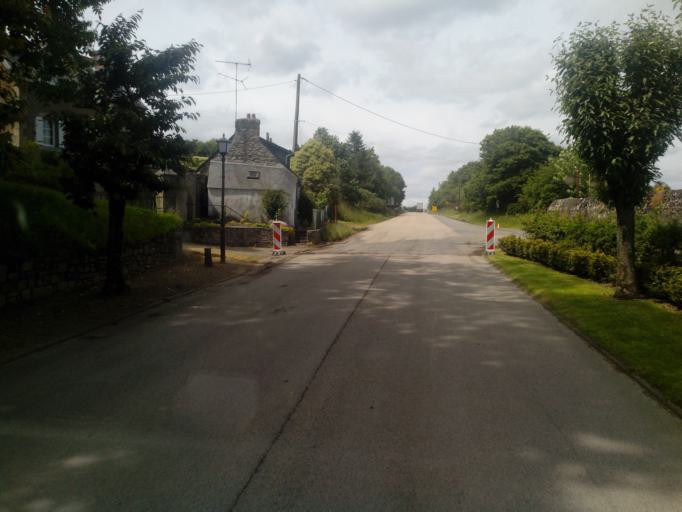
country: FR
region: Brittany
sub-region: Departement du Finistere
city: Guerlesquin
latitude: 48.5202
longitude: -3.5903
